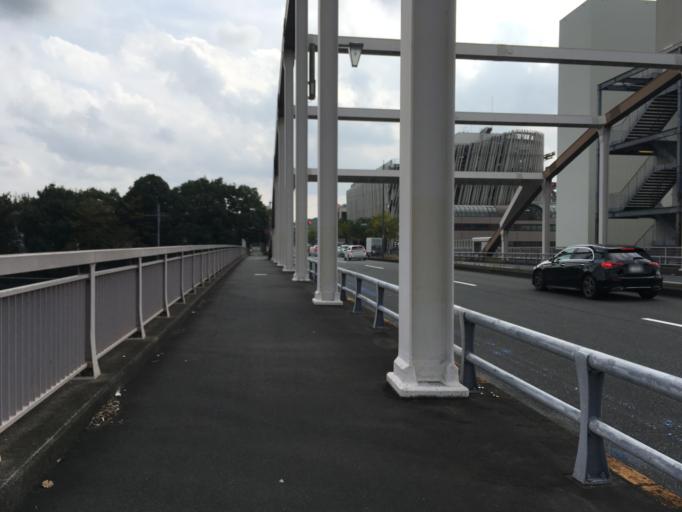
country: JP
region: Tokyo
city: Hino
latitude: 35.6154
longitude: 139.3808
